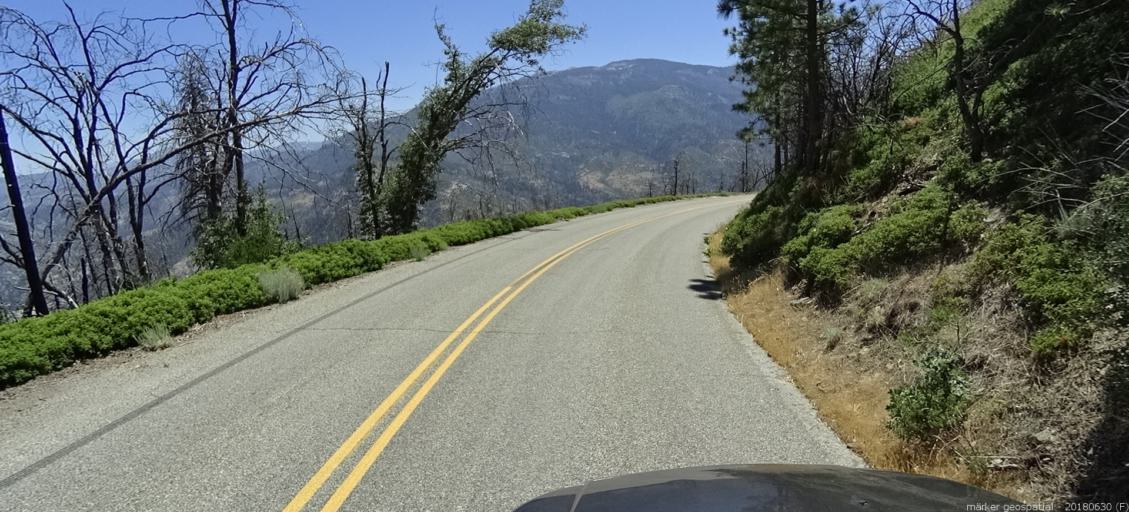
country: US
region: California
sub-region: Fresno County
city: Auberry
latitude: 37.2996
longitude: -119.3486
